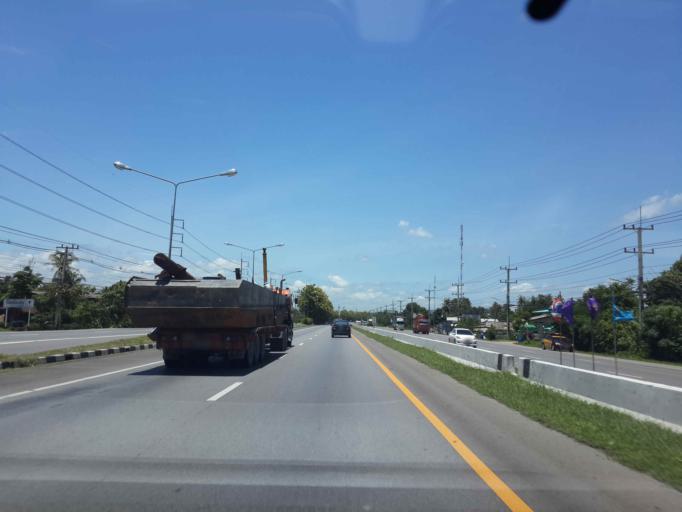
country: TH
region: Phetchaburi
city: Khao Yoi
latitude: 13.1597
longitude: 99.8457
